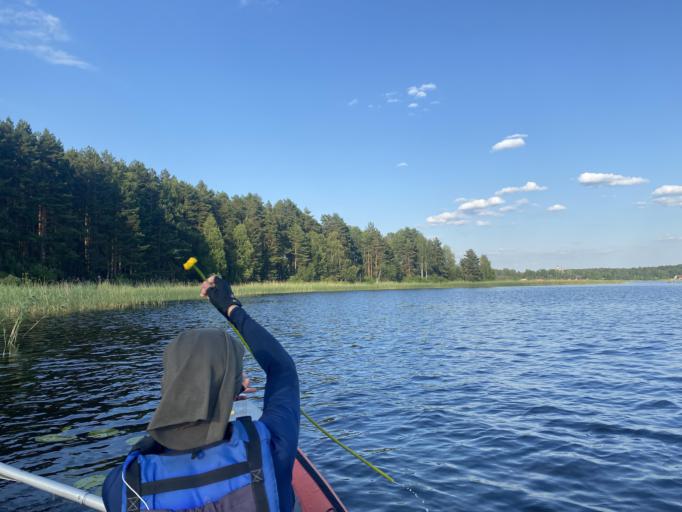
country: RU
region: Tverskaya
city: Ostashkov
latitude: 57.1002
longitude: 33.2415
